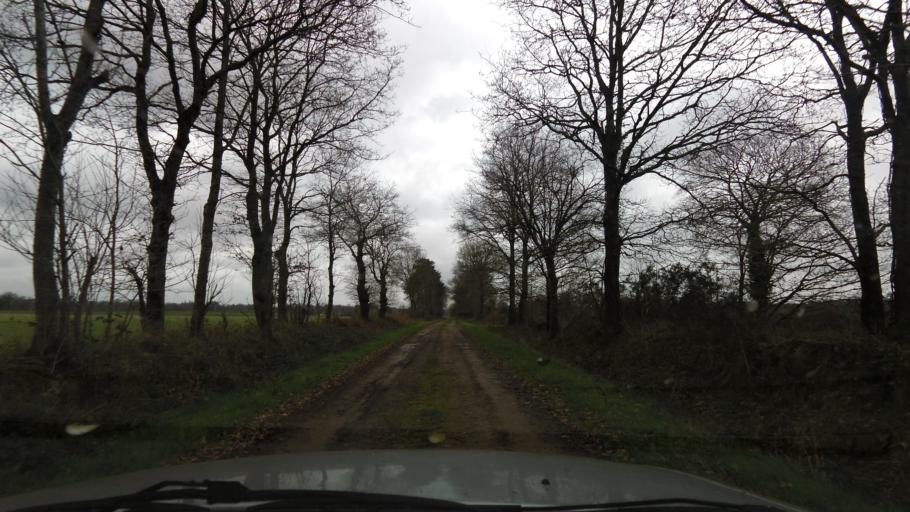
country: FR
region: Brittany
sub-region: Departement du Morbihan
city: Molac
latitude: 47.7659
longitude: -2.4665
